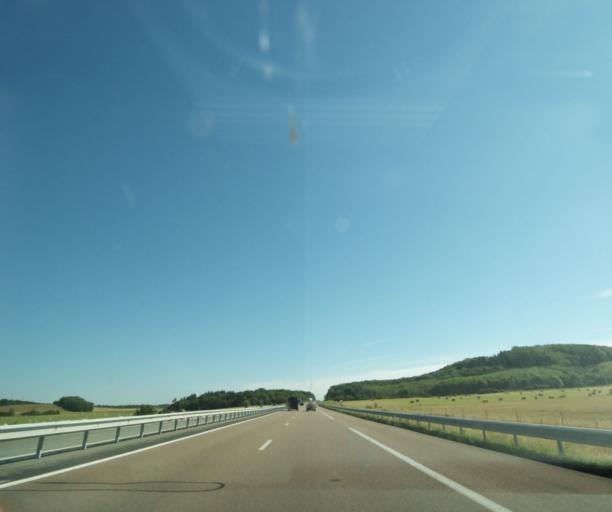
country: FR
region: Champagne-Ardenne
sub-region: Departement de la Haute-Marne
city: Saulxures
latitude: 48.0564
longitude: 5.5815
